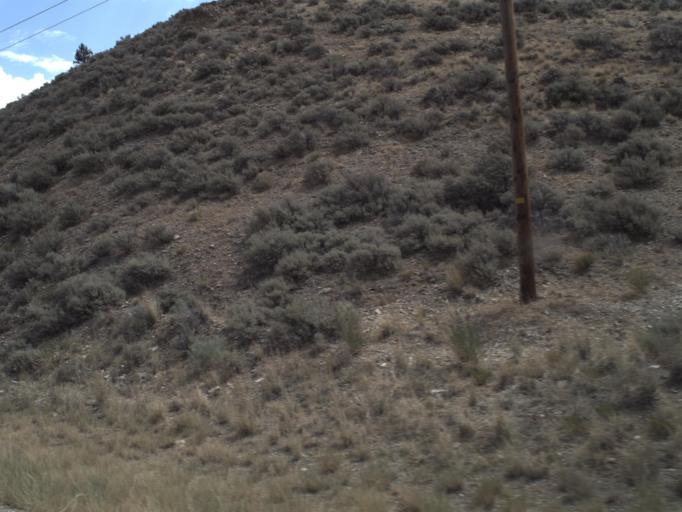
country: US
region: Utah
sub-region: Tooele County
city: Tooele
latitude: 40.4647
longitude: -112.3539
